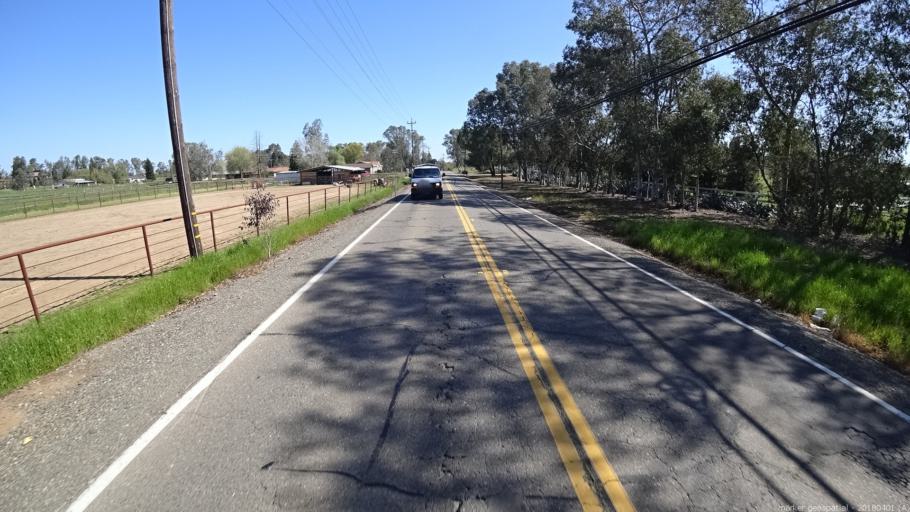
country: US
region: California
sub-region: Sacramento County
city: Wilton
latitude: 38.4071
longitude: -121.2477
